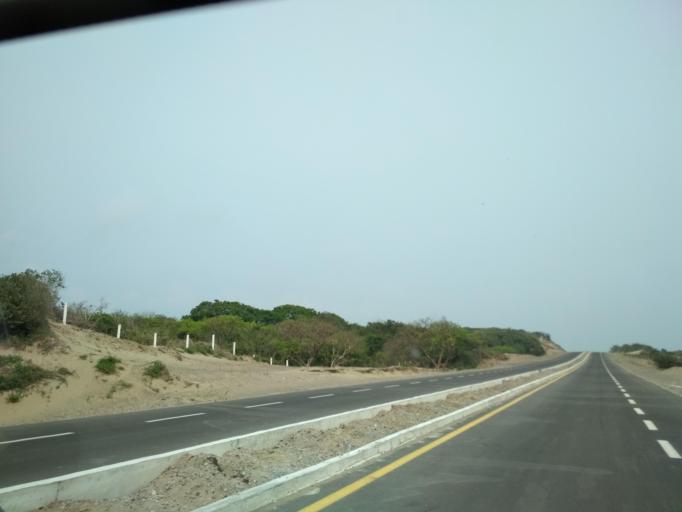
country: MX
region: Veracruz
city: Anton Lizardo
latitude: 19.0470
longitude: -95.9994
